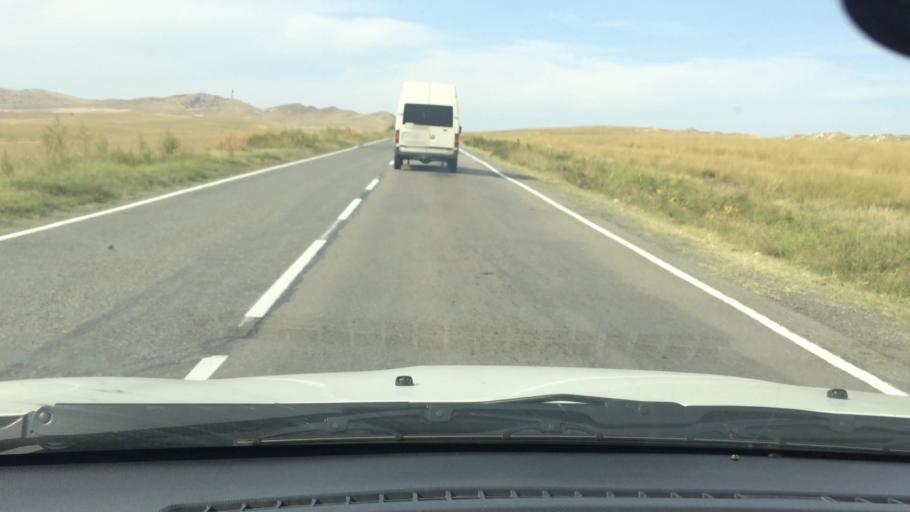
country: GE
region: Kvemo Kartli
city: Rust'avi
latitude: 41.5252
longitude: 44.9821
